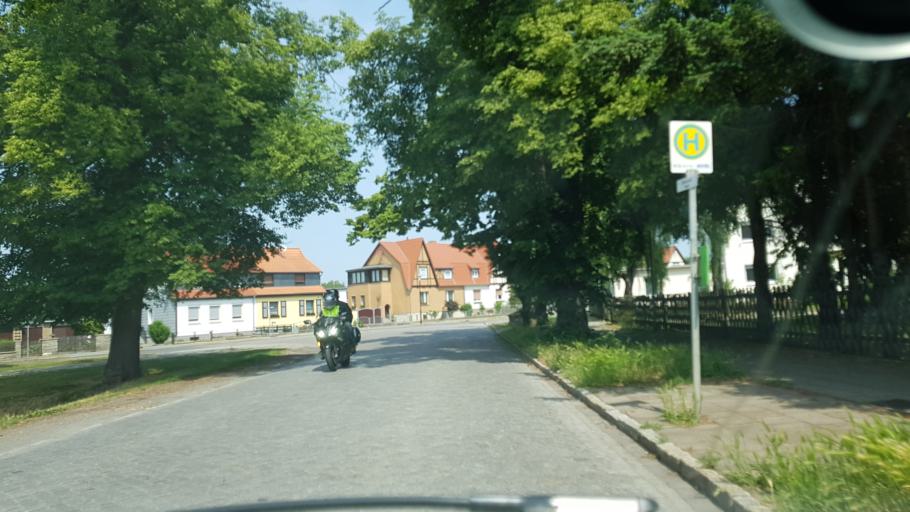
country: DE
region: Saxony-Anhalt
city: Osterwieck
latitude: 51.9708
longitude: 10.7042
